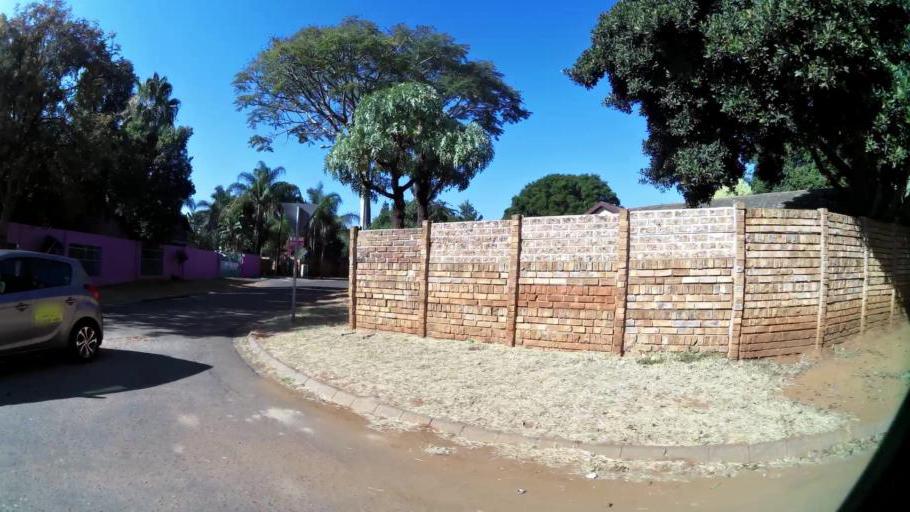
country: ZA
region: North-West
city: Ga-Rankuwa
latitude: -25.6662
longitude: 28.0903
